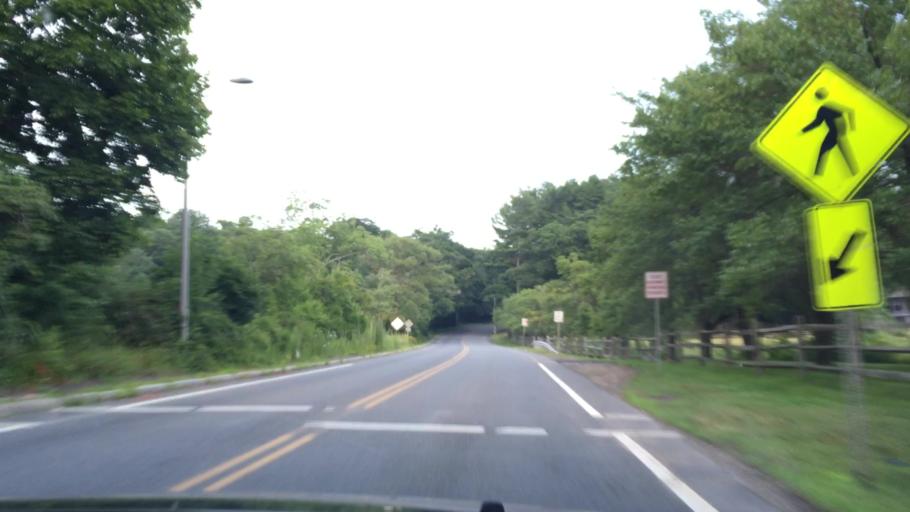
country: US
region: Massachusetts
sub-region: Essex County
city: Essex
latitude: 42.5795
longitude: -70.7538
